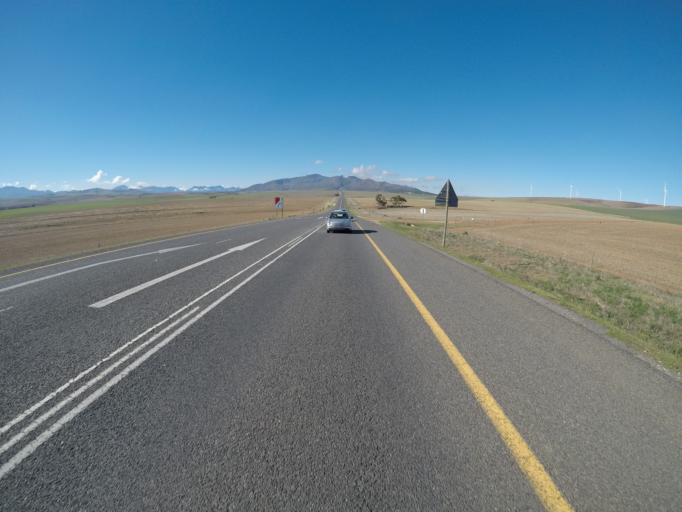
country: ZA
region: Western Cape
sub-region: Overberg District Municipality
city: Caledon
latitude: -34.2121
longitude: 19.3587
